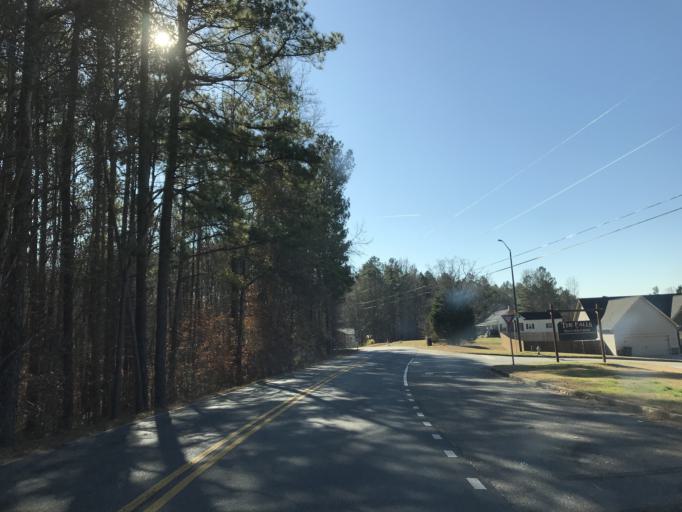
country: US
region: Georgia
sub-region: Paulding County
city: Dallas
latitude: 33.9882
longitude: -84.8937
